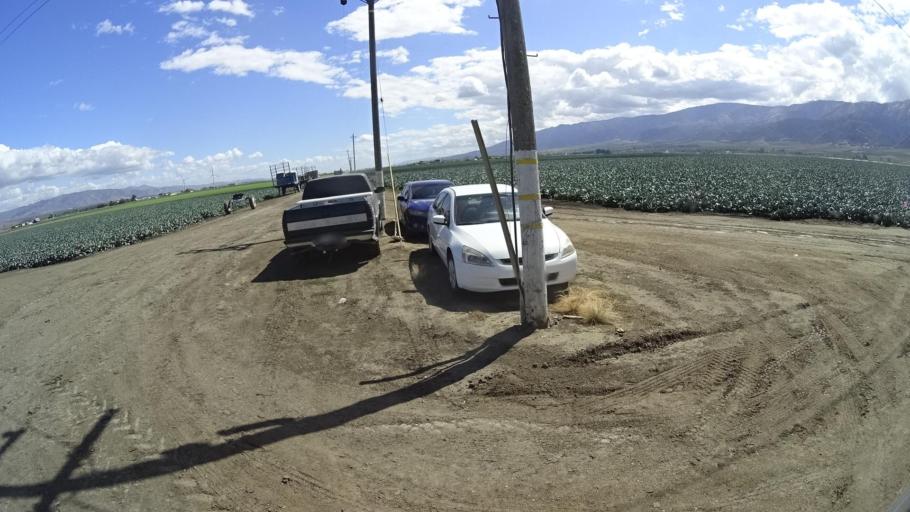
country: US
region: California
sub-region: Monterey County
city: Gonzales
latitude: 36.5148
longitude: -121.4796
